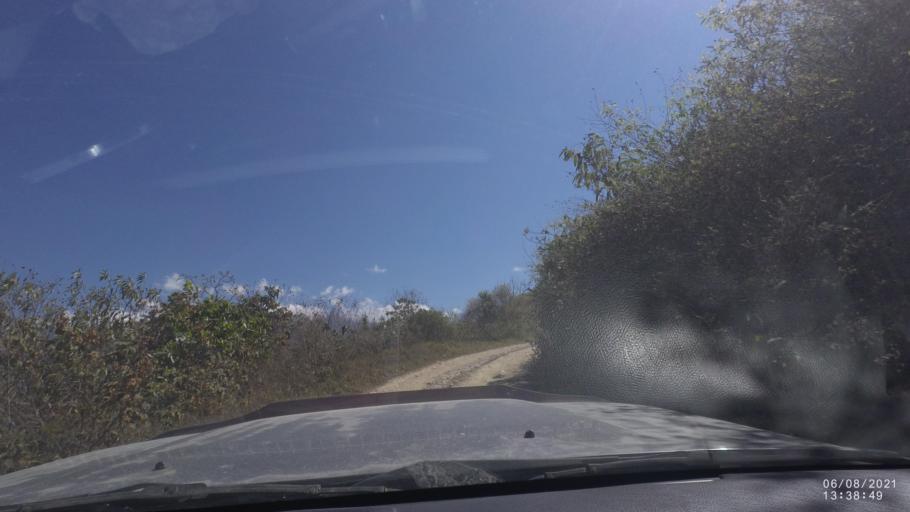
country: BO
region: La Paz
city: Quime
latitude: -16.6865
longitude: -66.7258
